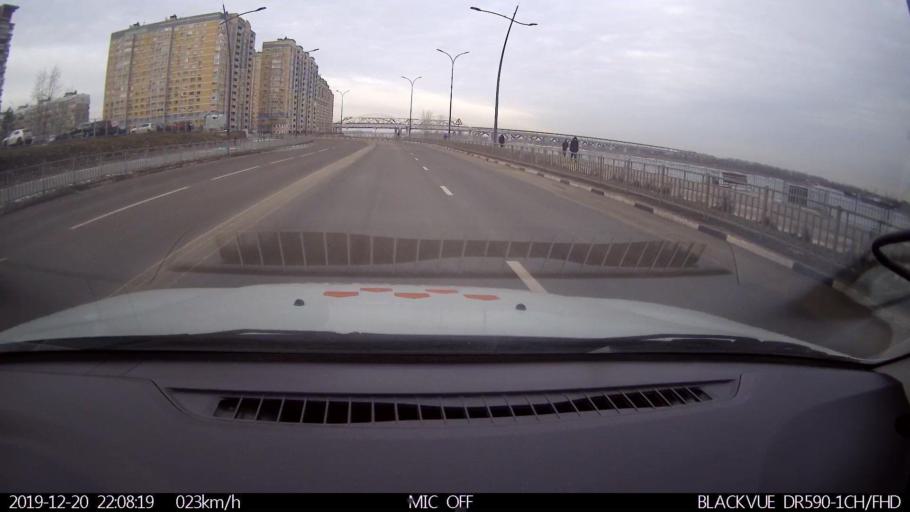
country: RU
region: Nizjnij Novgorod
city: Nizhniy Novgorod
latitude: 56.3463
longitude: 43.9401
